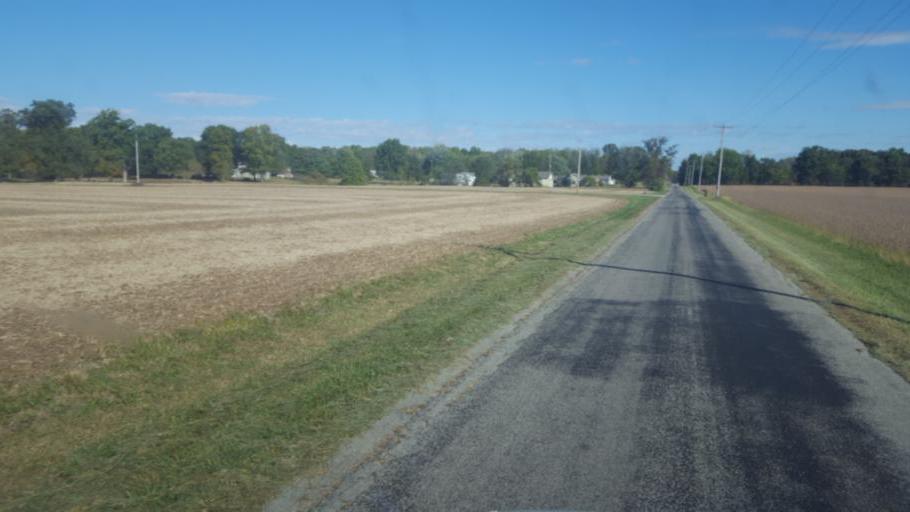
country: US
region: Ohio
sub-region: Wyandot County
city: Upper Sandusky
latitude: 40.7459
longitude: -83.2074
